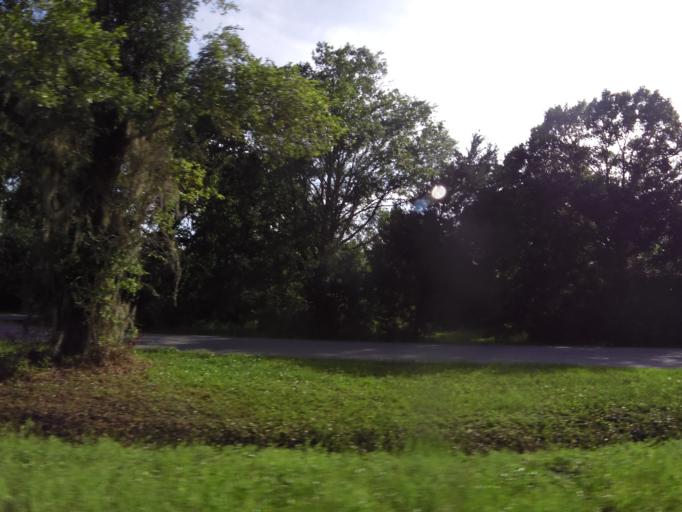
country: US
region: Florida
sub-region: Clay County
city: Green Cove Springs
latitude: 29.9993
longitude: -81.5431
